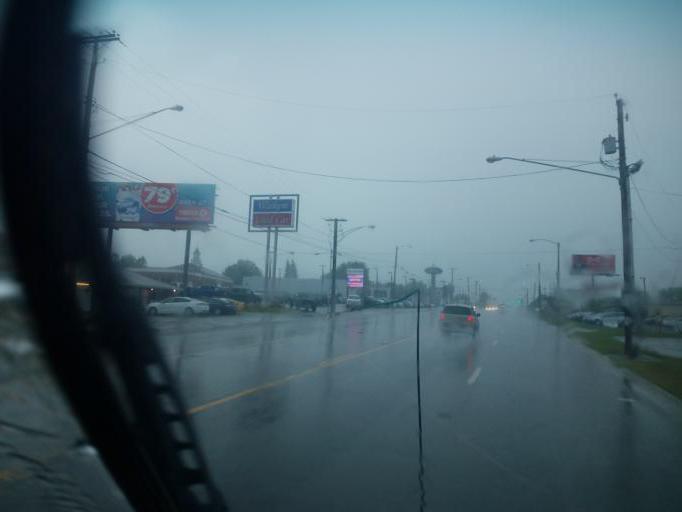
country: US
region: Ohio
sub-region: Stark County
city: Genoa
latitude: 40.7924
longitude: -81.4526
